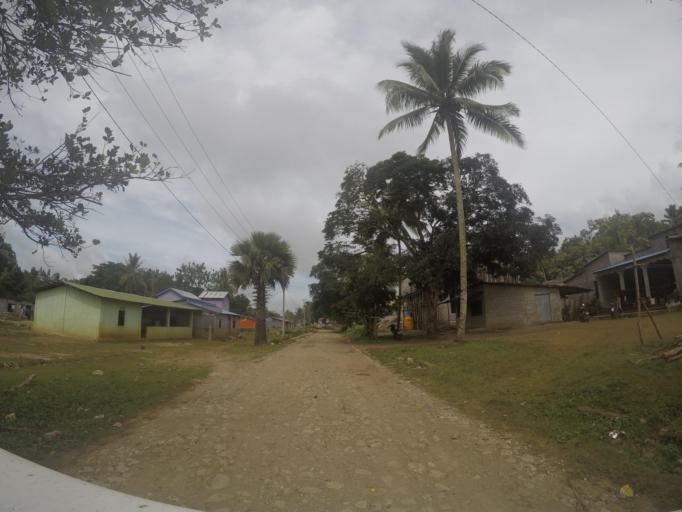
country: TL
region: Lautem
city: Lospalos
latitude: -8.5019
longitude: 126.9666
